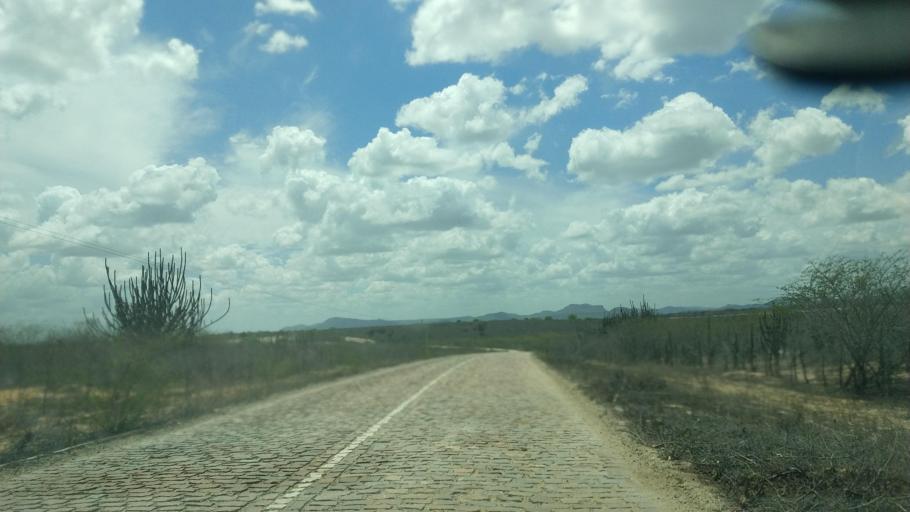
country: BR
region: Rio Grande do Norte
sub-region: Sao Paulo Do Potengi
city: Sao Paulo do Potengi
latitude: -5.9592
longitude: -35.8475
